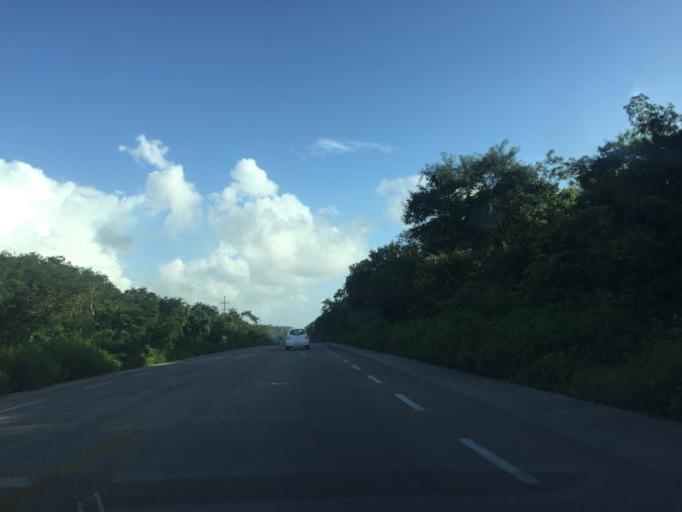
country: MX
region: Quintana Roo
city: Coba
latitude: 20.4949
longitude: -87.7071
